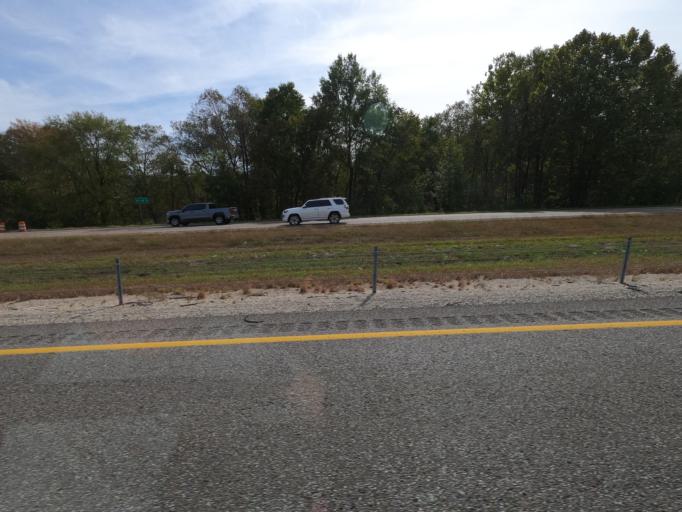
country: US
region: Tennessee
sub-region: Humphreys County
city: New Johnsonville
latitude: 35.8472
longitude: -88.0738
